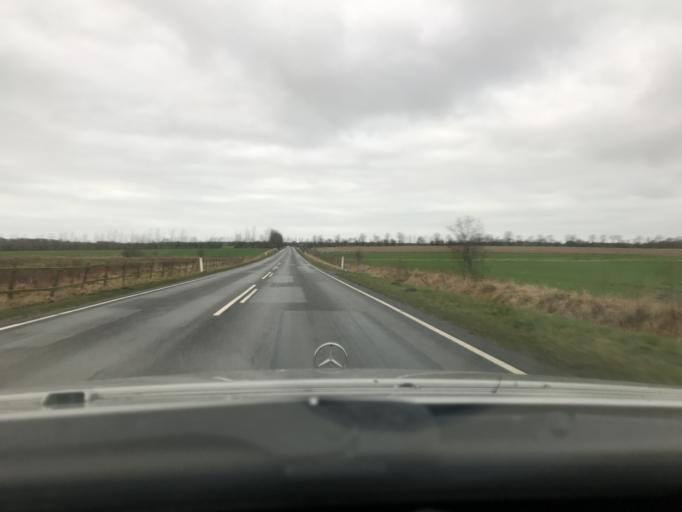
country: DK
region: South Denmark
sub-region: Tonder Kommune
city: Toftlund
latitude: 55.1781
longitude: 9.0155
